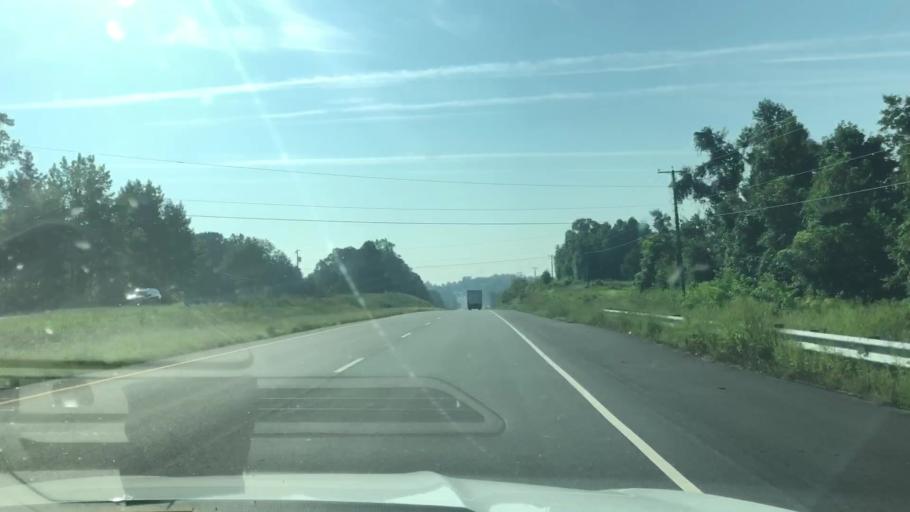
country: US
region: Virginia
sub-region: Richmond County
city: Warsaw
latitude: 37.9304
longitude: -76.7311
